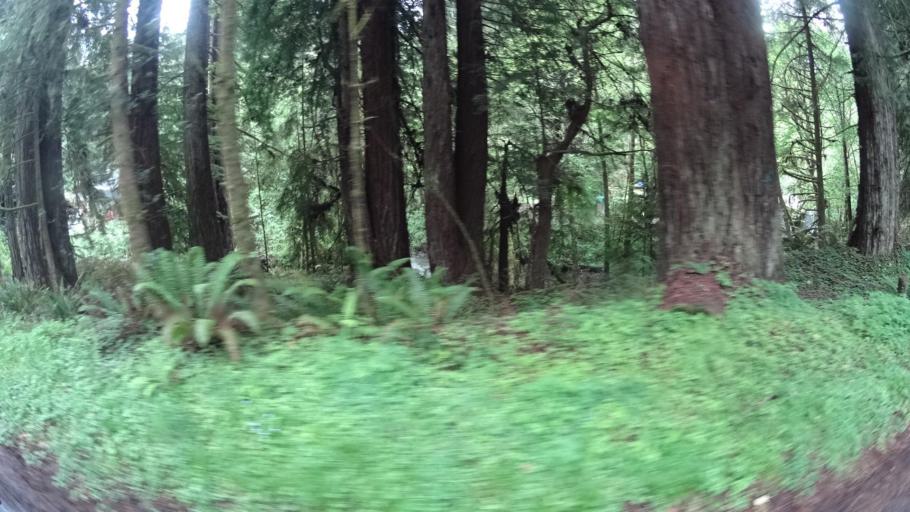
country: US
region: California
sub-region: Humboldt County
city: Bayside
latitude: 40.8274
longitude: -124.0376
